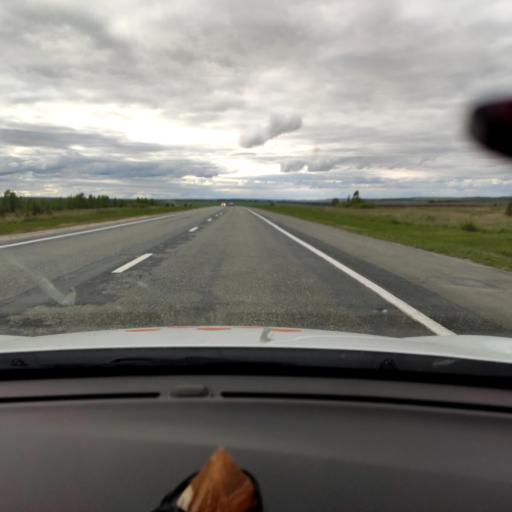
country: RU
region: Tatarstan
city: Laishevo
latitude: 55.5046
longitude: 49.8278
